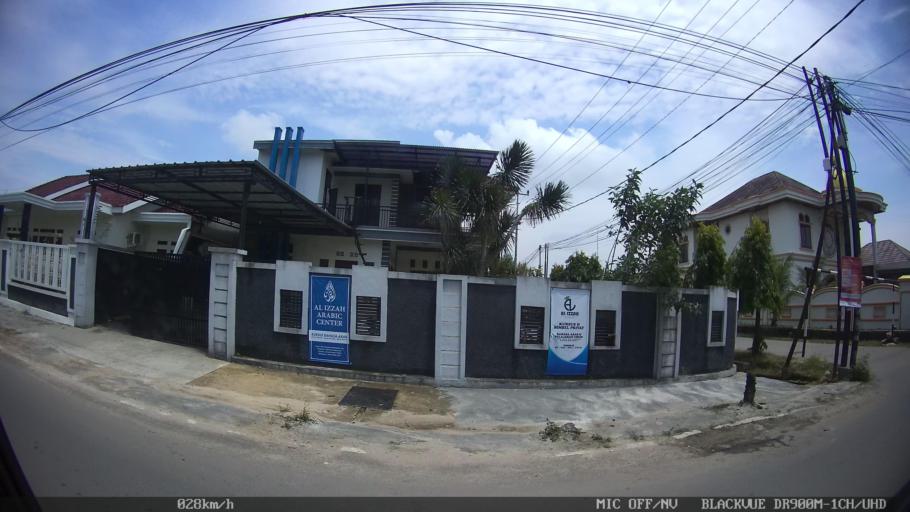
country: ID
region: Lampung
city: Kedaton
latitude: -5.3722
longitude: 105.3008
